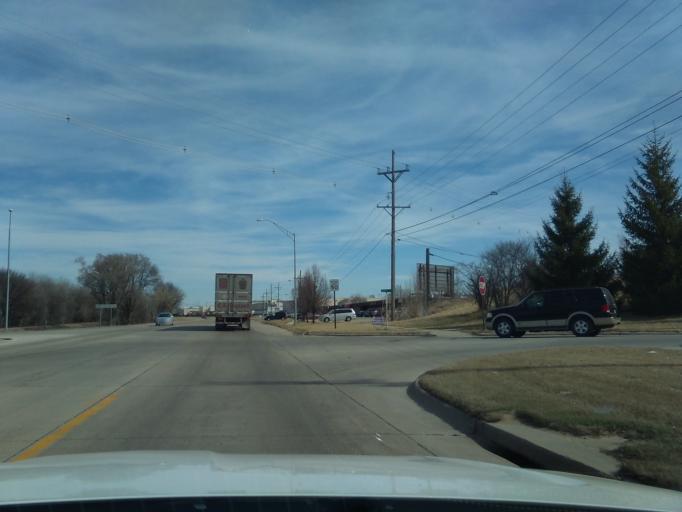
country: US
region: Nebraska
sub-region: Saline County
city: Crete
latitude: 40.6322
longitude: -96.9523
